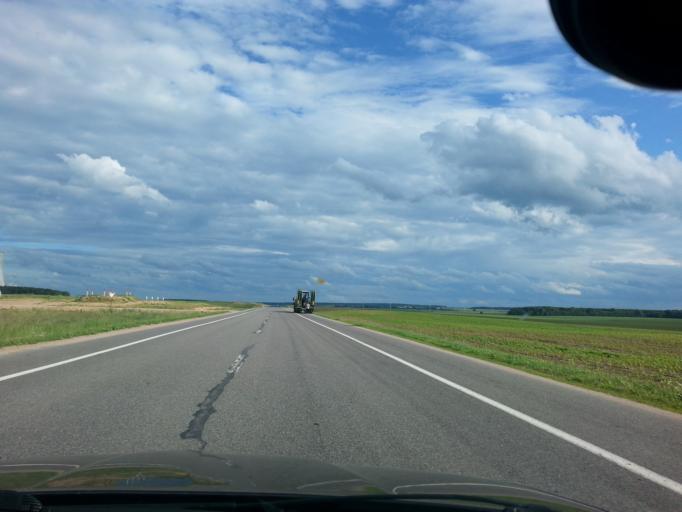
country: BY
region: Grodnenskaya
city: Astravyets
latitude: 54.7742
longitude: 26.0582
